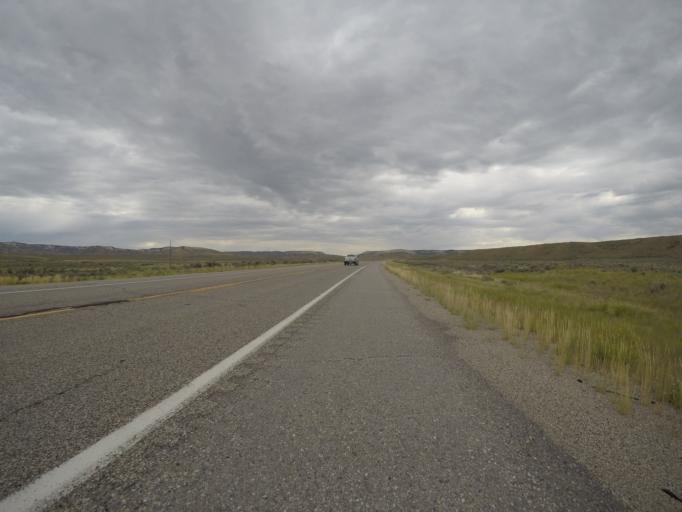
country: US
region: Wyoming
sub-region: Lincoln County
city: Kemmerer
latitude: 41.8158
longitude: -110.7170
